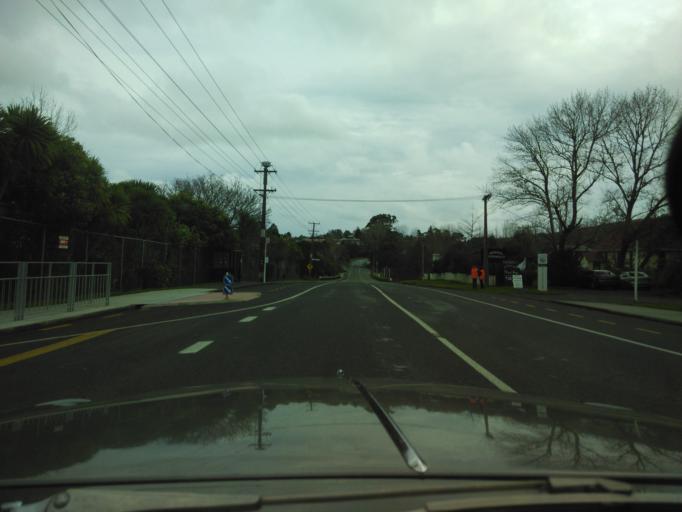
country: NZ
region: Auckland
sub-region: Auckland
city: Muriwai Beach
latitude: -36.7693
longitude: 174.4919
